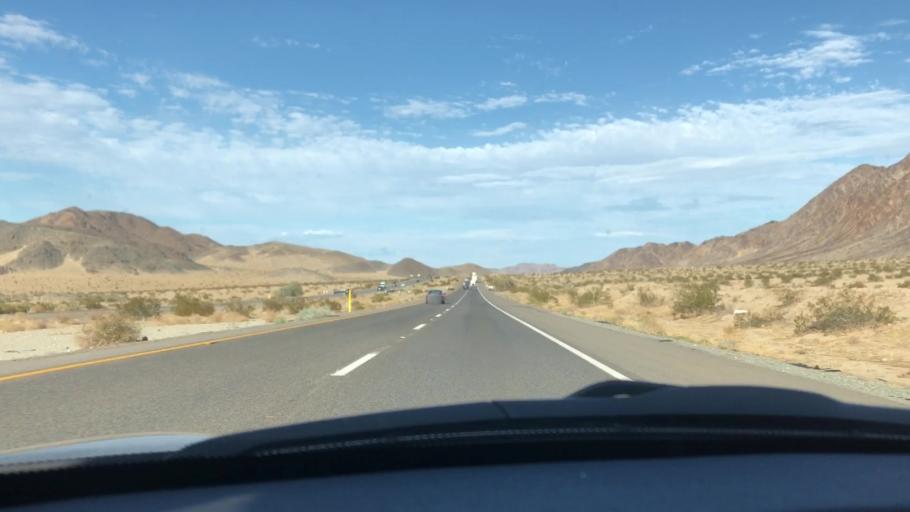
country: US
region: California
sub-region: San Bernardino County
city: Fort Irwin
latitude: 35.0856
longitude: -116.3552
